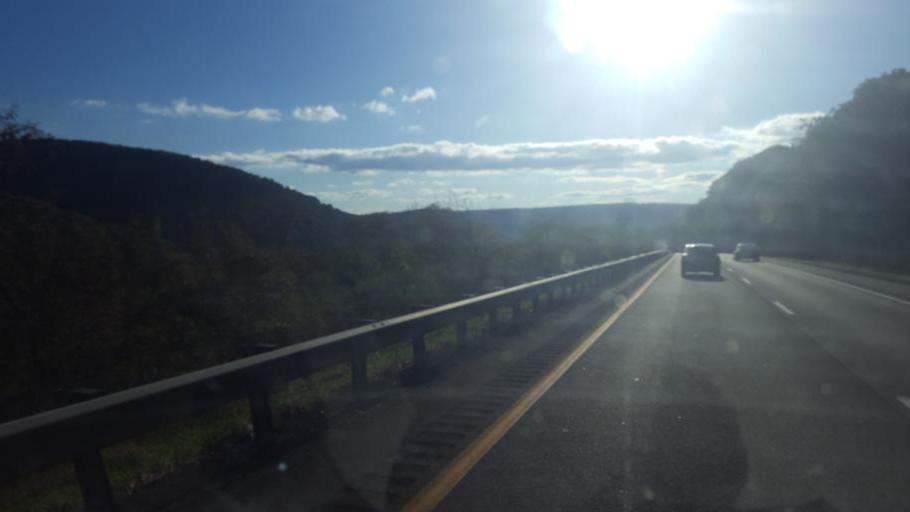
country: US
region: Maryland
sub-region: Allegany County
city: Cresaptown
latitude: 39.6396
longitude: -78.8652
